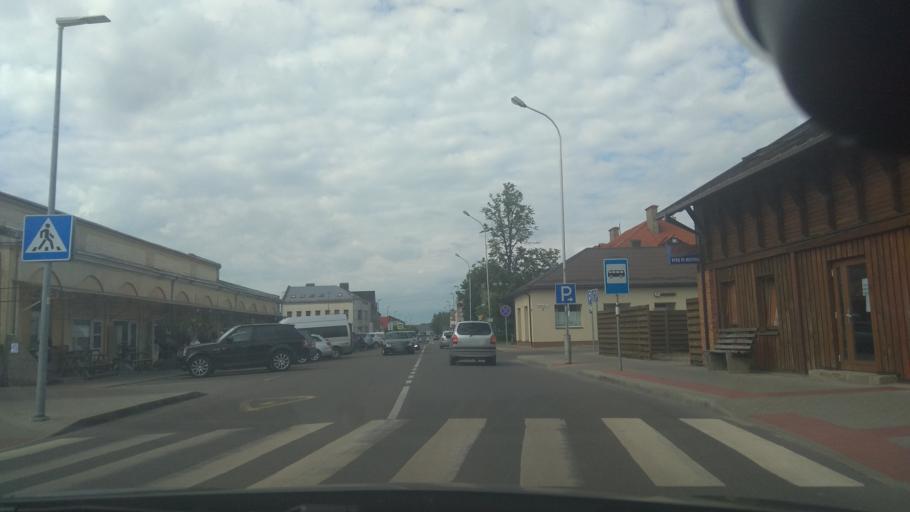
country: LT
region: Marijampoles apskritis
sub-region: Marijampole Municipality
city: Marijampole
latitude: 54.5535
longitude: 23.3538
